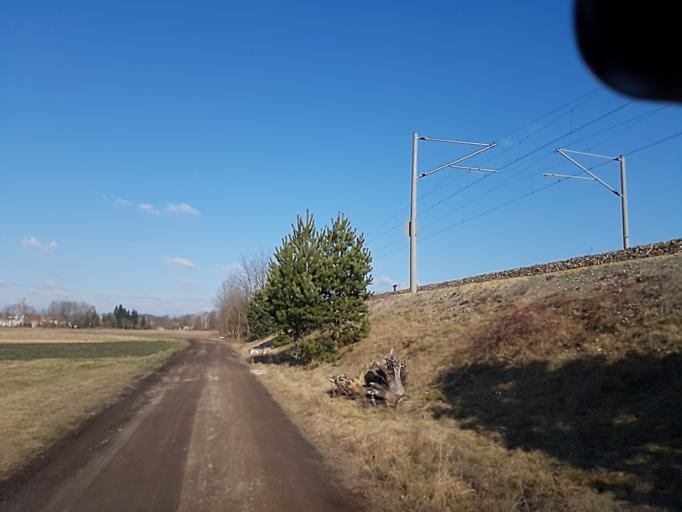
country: DE
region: Brandenburg
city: Doberlug-Kirchhain
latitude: 51.6127
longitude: 13.5626
